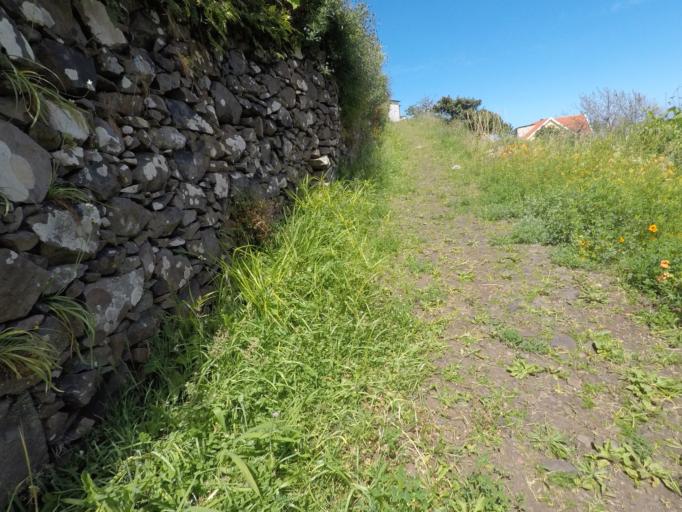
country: PT
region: Madeira
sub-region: Sao Vicente
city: Sao Vicente
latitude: 32.8259
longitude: -16.9728
